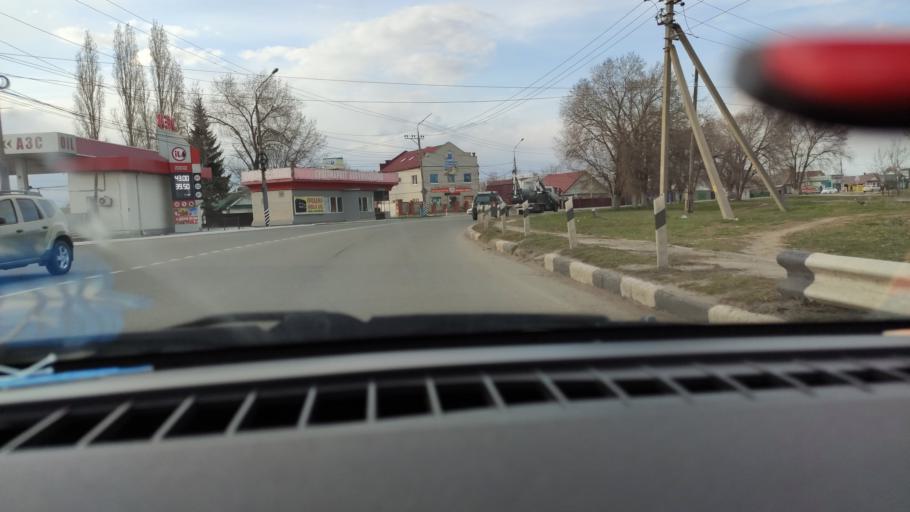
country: RU
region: Saratov
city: Privolzhskiy
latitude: 51.4265
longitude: 46.0482
